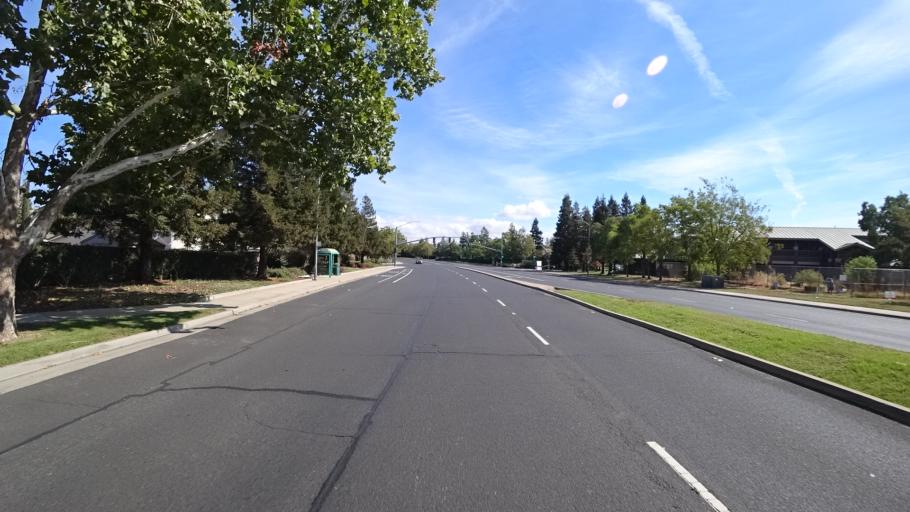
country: US
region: California
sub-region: Sacramento County
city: Laguna
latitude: 38.4308
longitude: -121.4269
